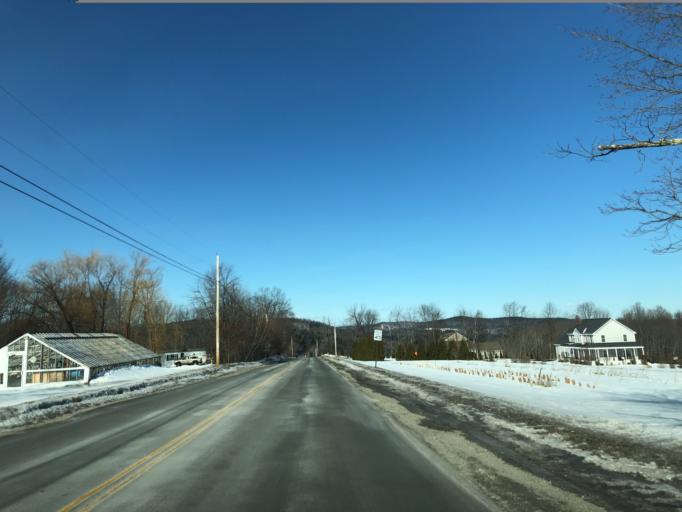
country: US
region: Maine
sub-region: Androscoggin County
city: Minot
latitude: 44.1345
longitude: -70.3165
